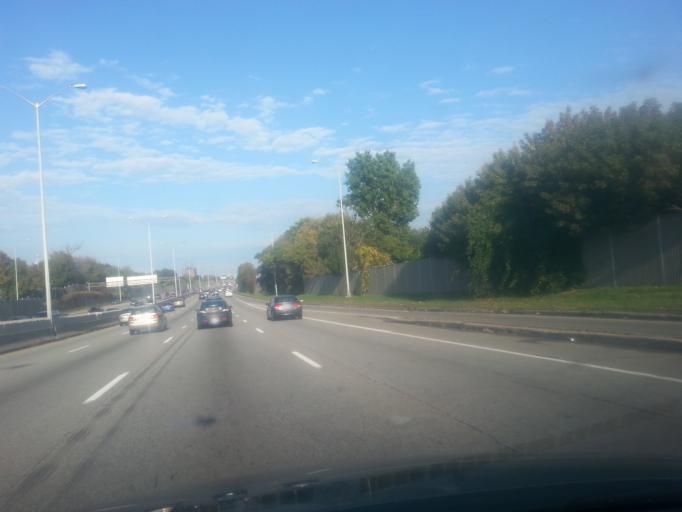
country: CA
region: Ontario
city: Ottawa
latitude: 45.3979
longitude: -75.7251
